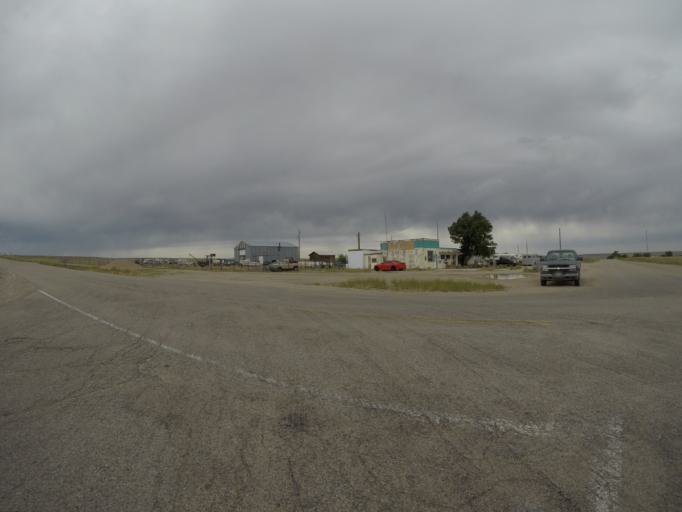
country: US
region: Wyoming
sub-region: Lincoln County
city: Kemmerer
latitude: 41.9802
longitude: -110.0616
